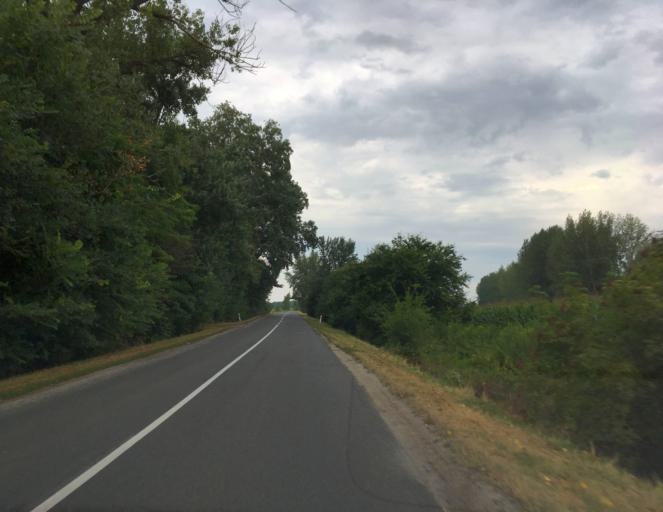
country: SK
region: Trnavsky
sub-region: Okres Dunajska Streda
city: Velky Meder
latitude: 47.9023
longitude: 17.6797
